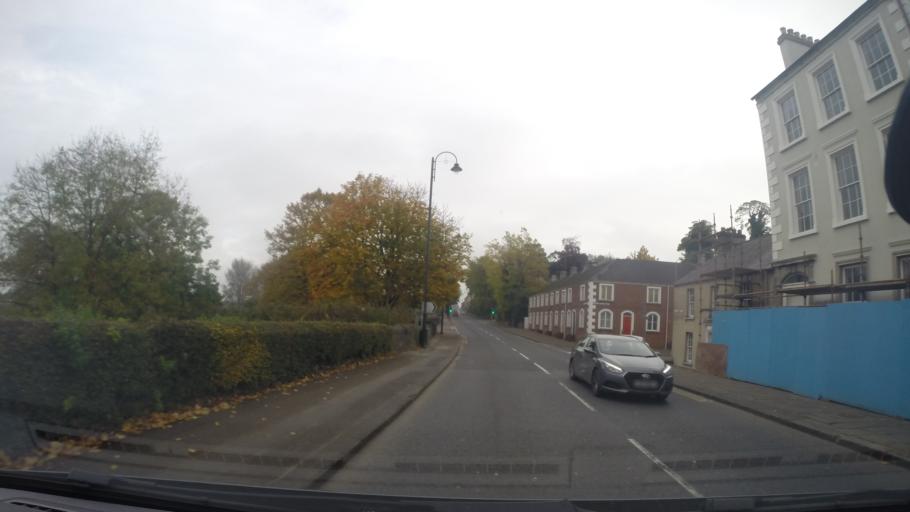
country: GB
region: Northern Ireland
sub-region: Fermanagh District
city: Enniskillen
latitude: 54.3490
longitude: -7.6511
